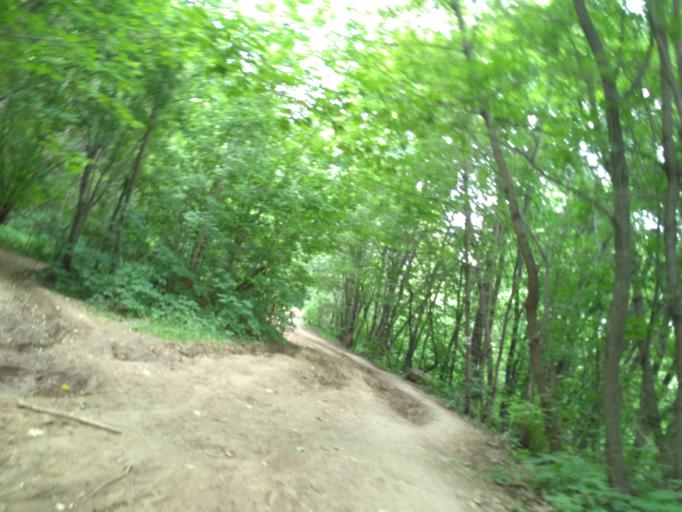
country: RU
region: Nizjnij Novgorod
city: Nizhniy Novgorod
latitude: 56.2813
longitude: 43.9705
